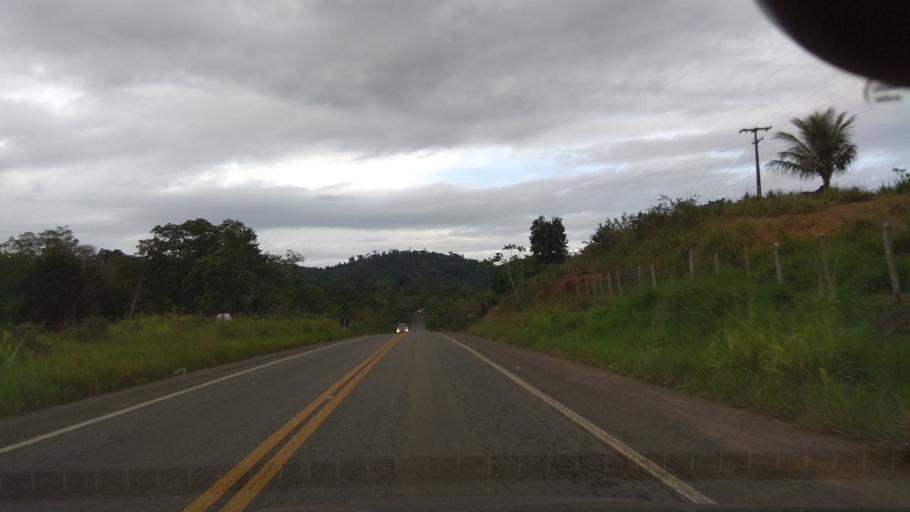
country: BR
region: Bahia
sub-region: Ubata
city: Ubata
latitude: -14.2291
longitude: -39.4447
